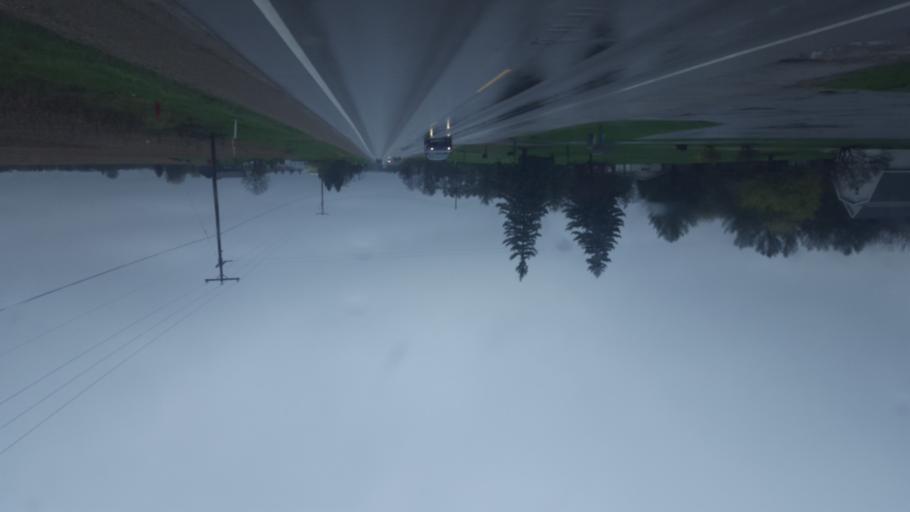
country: US
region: Michigan
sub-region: Isabella County
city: Mount Pleasant
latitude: 43.5968
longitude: -84.8335
